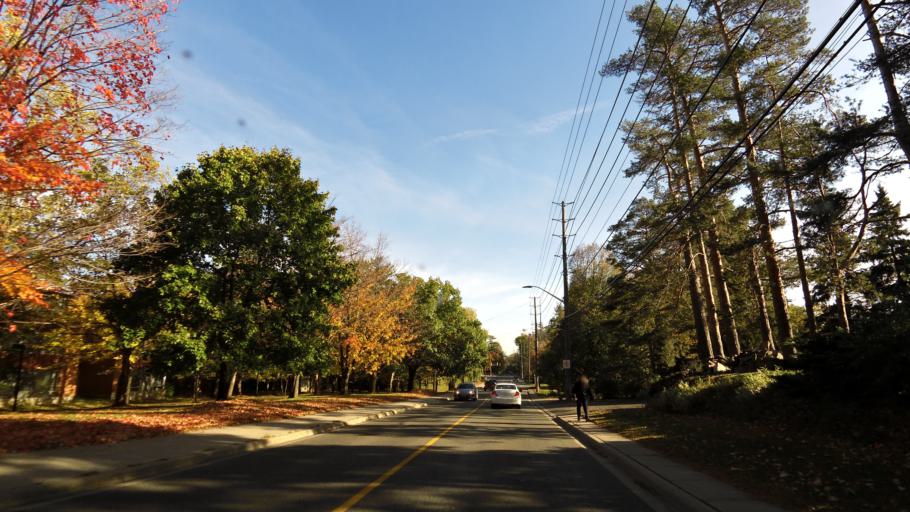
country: CA
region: Ontario
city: Mississauga
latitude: 43.5483
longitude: -79.6681
